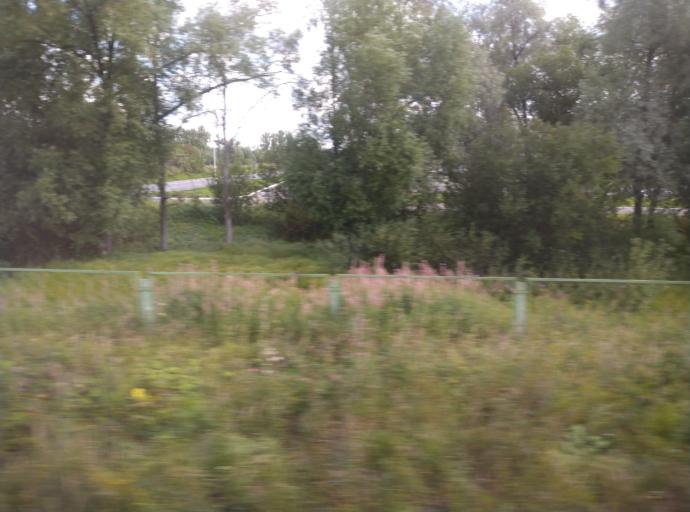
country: RU
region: St.-Petersburg
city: Kolpino
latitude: 59.7397
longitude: 30.6268
